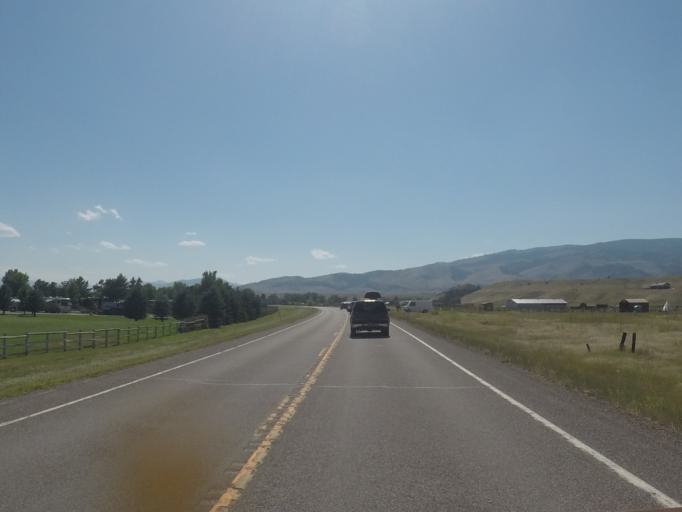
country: US
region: Montana
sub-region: Park County
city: Livingston
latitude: 45.4181
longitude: -110.6819
